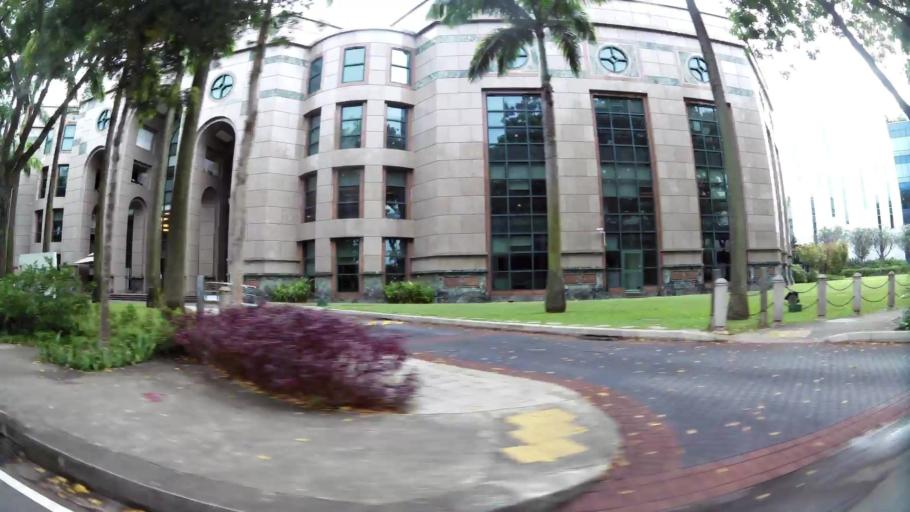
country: SG
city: Singapore
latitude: 1.2907
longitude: 103.7882
